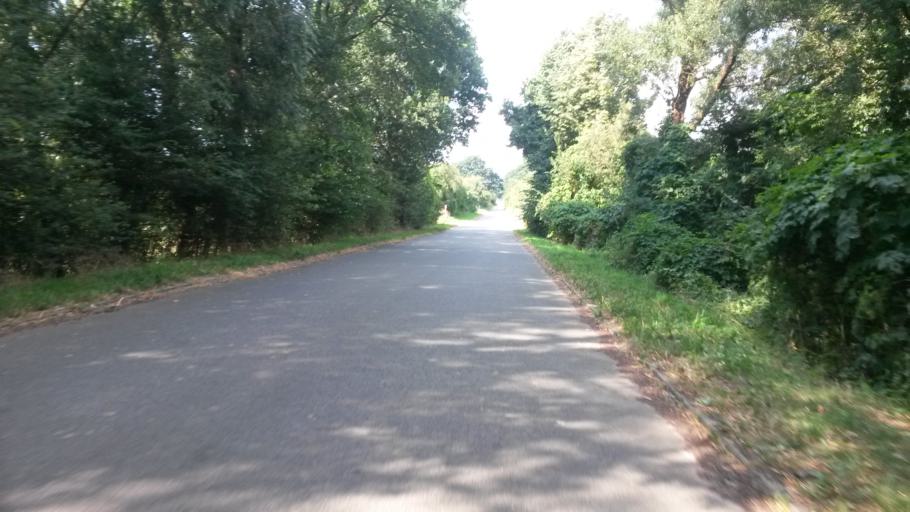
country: DE
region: Lower Saxony
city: Riede
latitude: 53.0306
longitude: 8.9336
